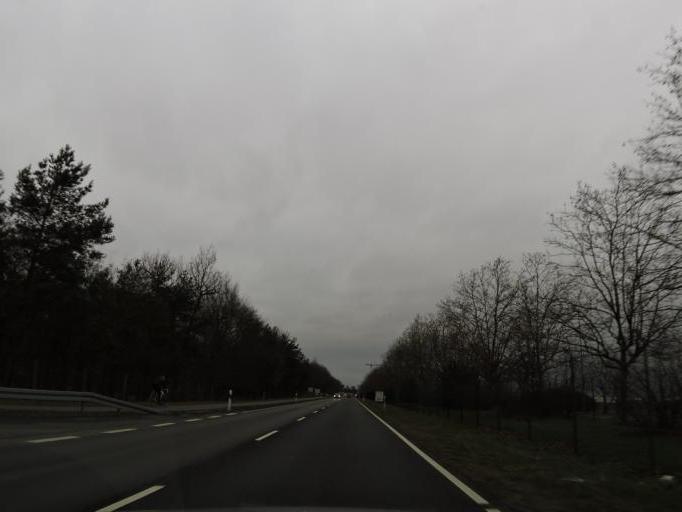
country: DE
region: Hesse
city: Kelsterbach
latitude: 50.0271
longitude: 8.5196
